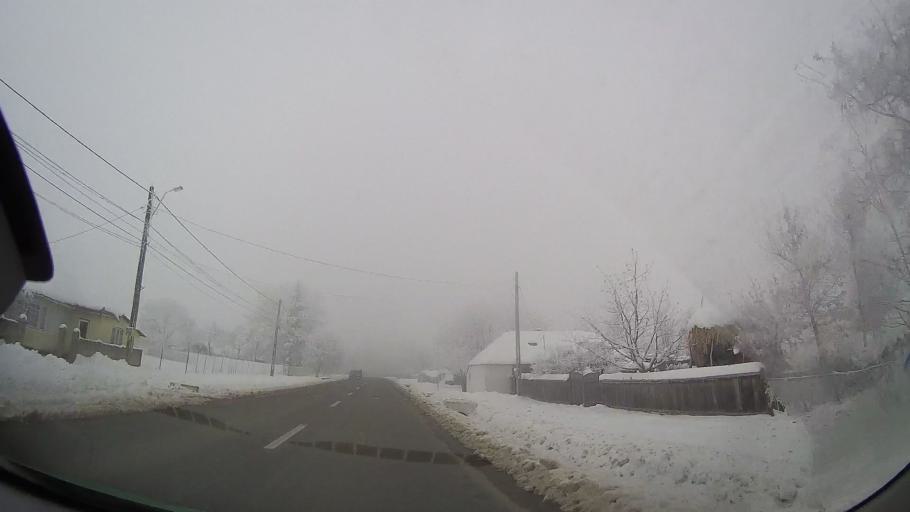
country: RO
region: Iasi
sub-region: Comuna Mogosesti-Siret
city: Mogosesti-Siret
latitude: 47.1634
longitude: 26.7712
